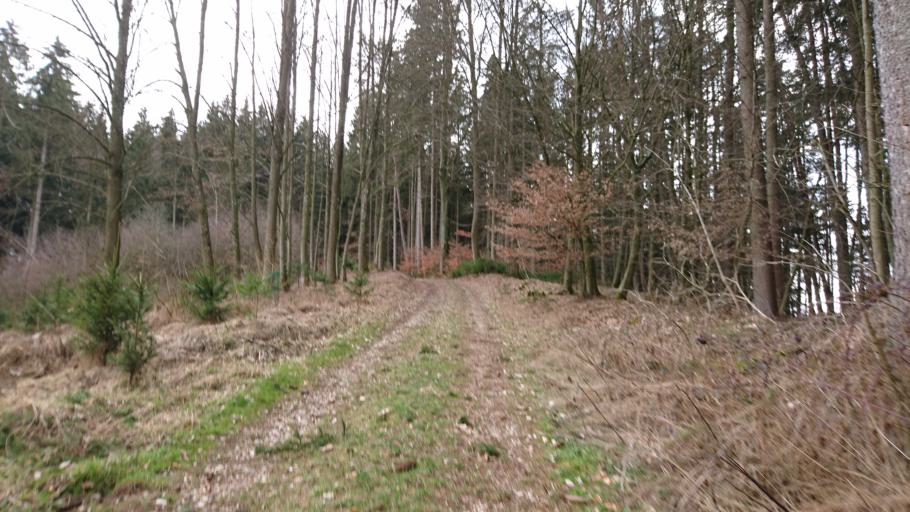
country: DE
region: Bavaria
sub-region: Swabia
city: Zusmarshausen
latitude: 48.4303
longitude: 10.5840
